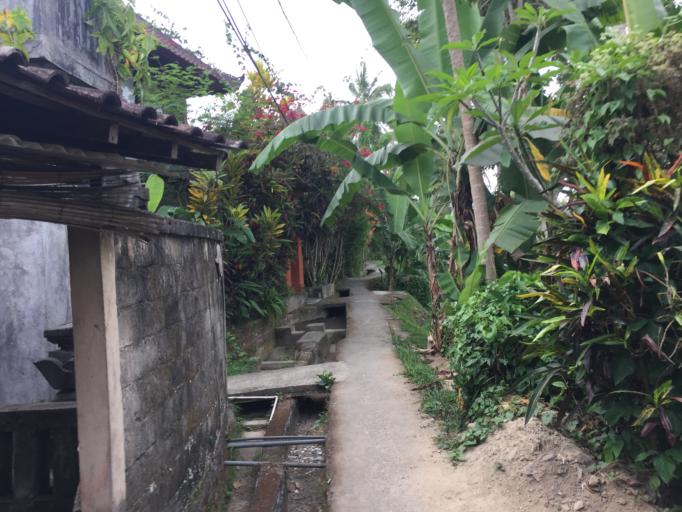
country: ID
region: Bali
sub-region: Kabupaten Gianyar
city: Ubud
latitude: -8.5017
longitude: 115.2518
